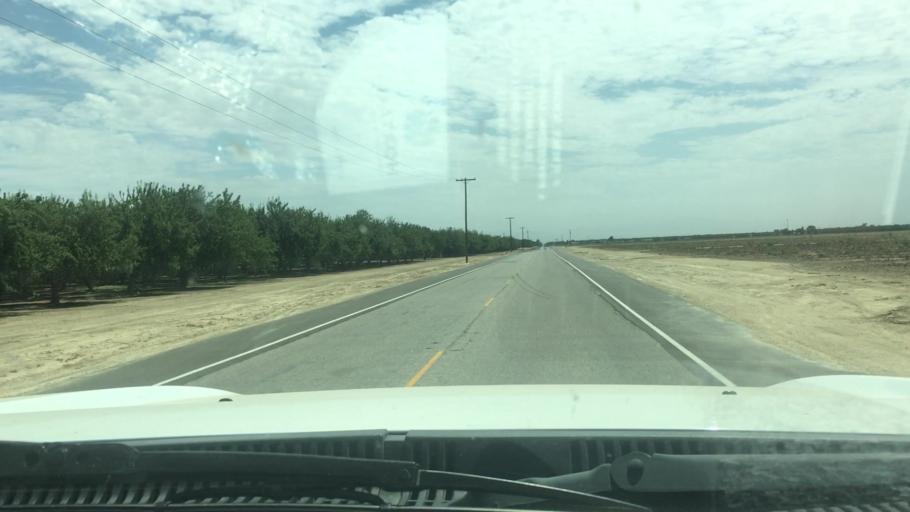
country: US
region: California
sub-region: Kern County
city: Wasco
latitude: 35.5579
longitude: -119.4002
